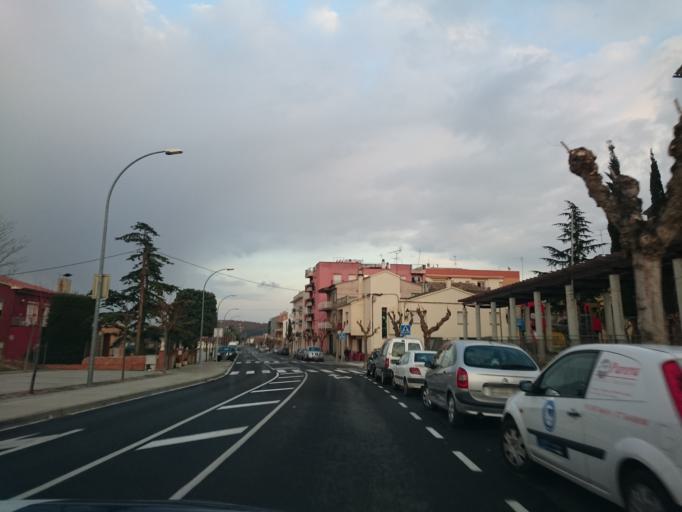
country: ES
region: Catalonia
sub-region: Provincia de Barcelona
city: Sant Marti Sarroca
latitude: 41.3877
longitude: 1.5722
